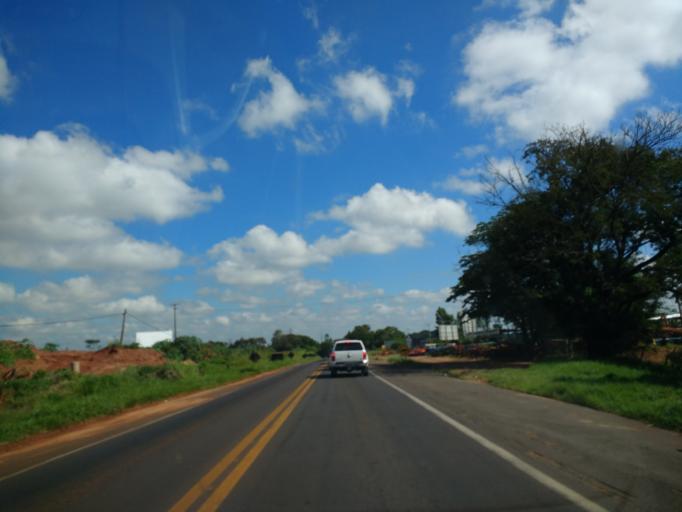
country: BR
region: Parana
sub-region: Umuarama
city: Umuarama
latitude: -23.8139
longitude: -53.3282
